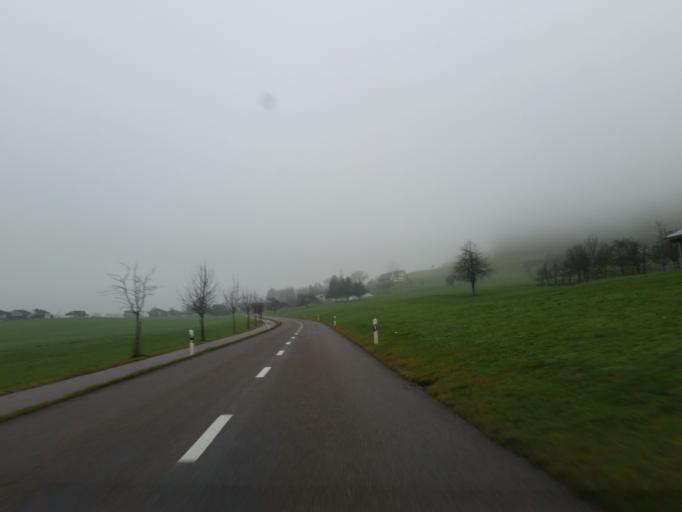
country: CH
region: Saint Gallen
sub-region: Wahlkreis Wil
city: Niederhelfenschwil
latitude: 47.4831
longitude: 9.1505
